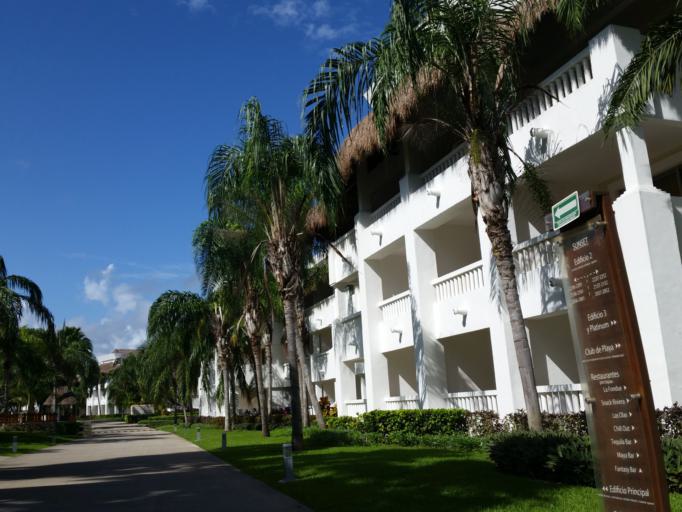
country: MX
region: Quintana Roo
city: Playa del Carmen
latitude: 20.6694
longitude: -87.0317
